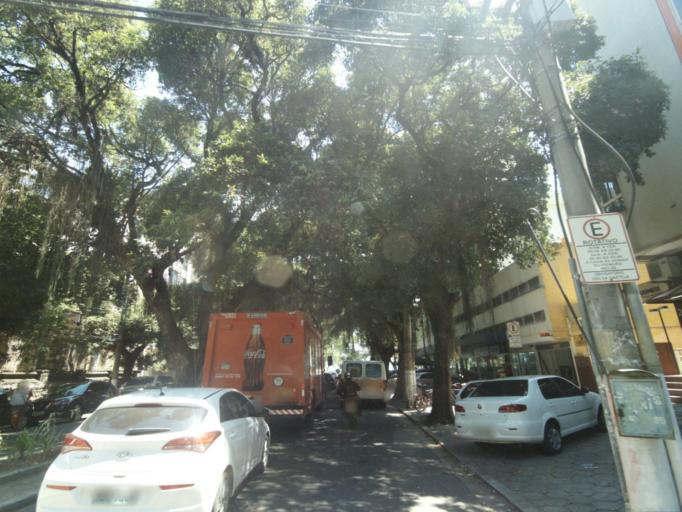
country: BR
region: Rio de Janeiro
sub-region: Niteroi
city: Niteroi
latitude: -22.9206
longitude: -43.0930
